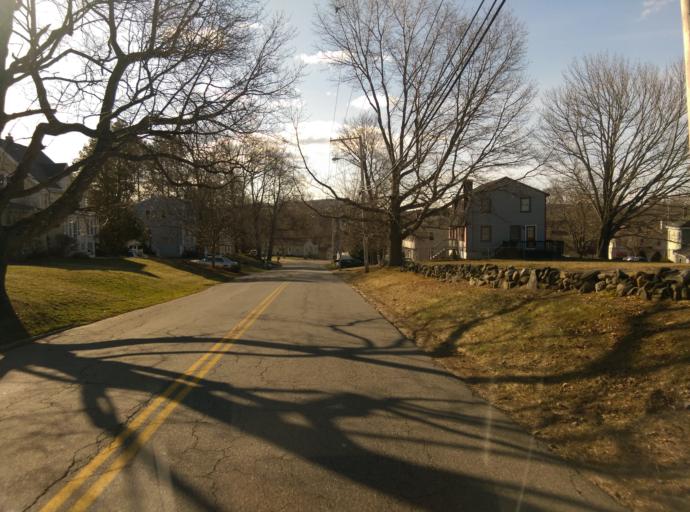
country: US
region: Massachusetts
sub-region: Essex County
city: Haverhill
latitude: 42.7499
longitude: -71.1130
